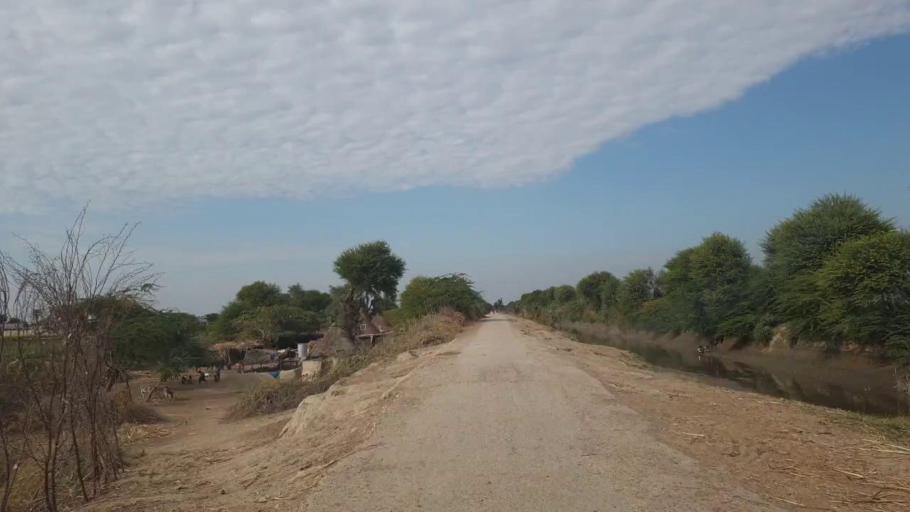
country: PK
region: Sindh
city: Sinjhoro
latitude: 26.0619
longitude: 68.8734
